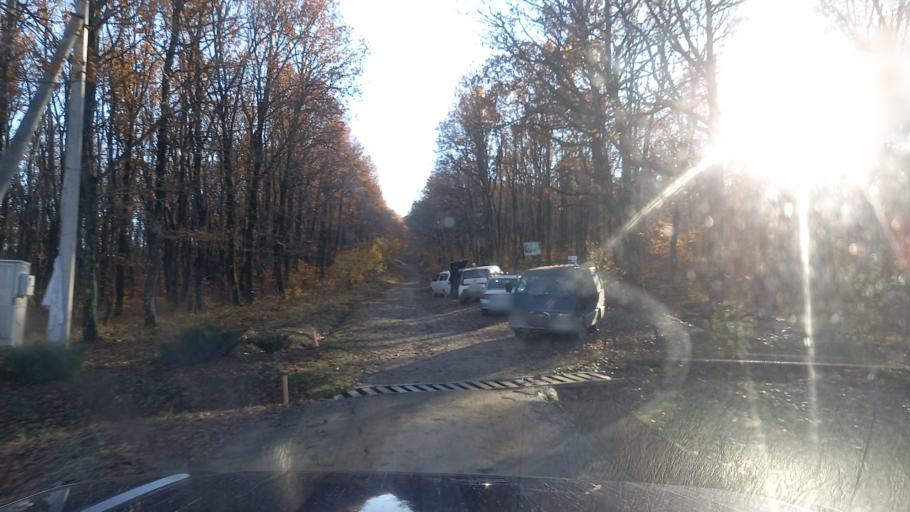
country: RU
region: Krasnodarskiy
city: Goryachiy Klyuch
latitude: 44.6180
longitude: 39.1045
